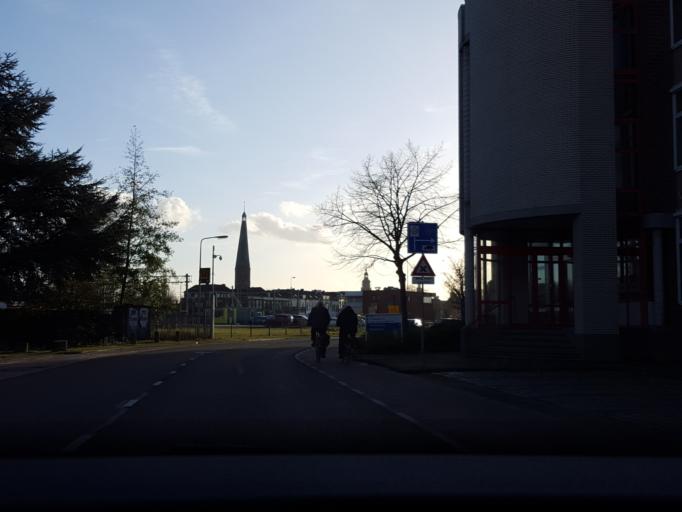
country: NL
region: Gelderland
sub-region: Gemeente Zutphen
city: Zutphen
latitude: 52.1494
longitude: 6.1988
